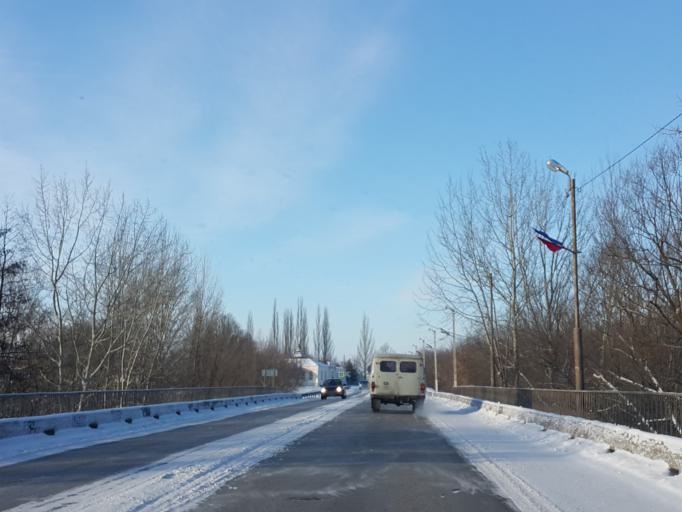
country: RU
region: Tambov
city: Znamenka
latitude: 52.4179
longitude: 41.4345
